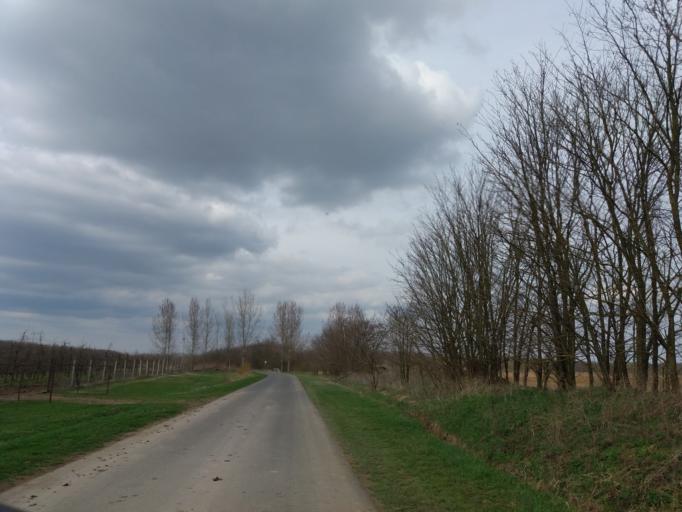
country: HU
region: Szabolcs-Szatmar-Bereg
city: Petnehaza
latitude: 48.0659
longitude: 22.0463
